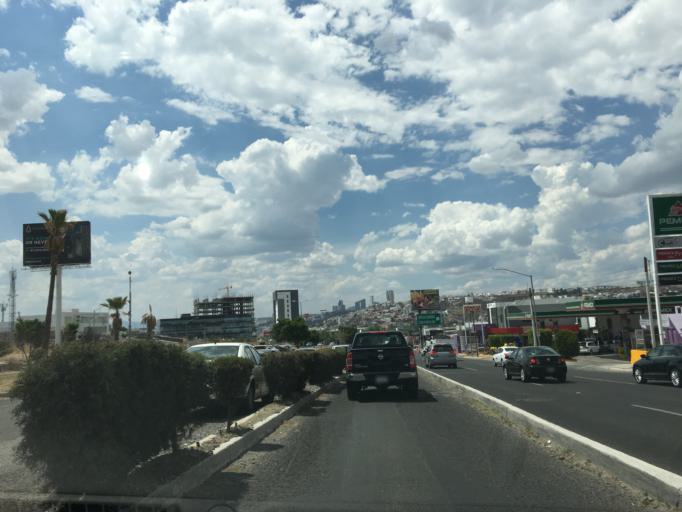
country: MX
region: Queretaro
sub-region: Queretaro
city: Santiago de Queretaro
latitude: 20.5753
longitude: -100.3605
